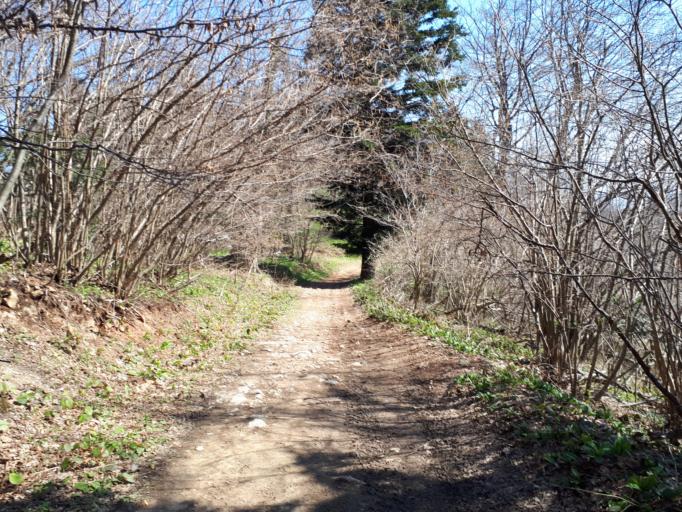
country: HR
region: Varazdinska
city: Ivanec
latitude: 46.1773
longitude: 16.1399
